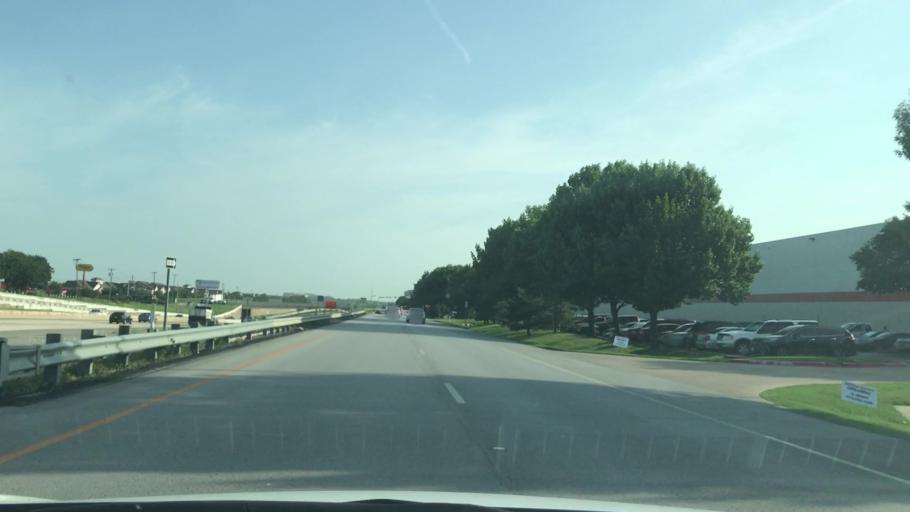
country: US
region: Texas
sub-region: Tarrant County
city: Euless
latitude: 32.7898
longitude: -97.0576
